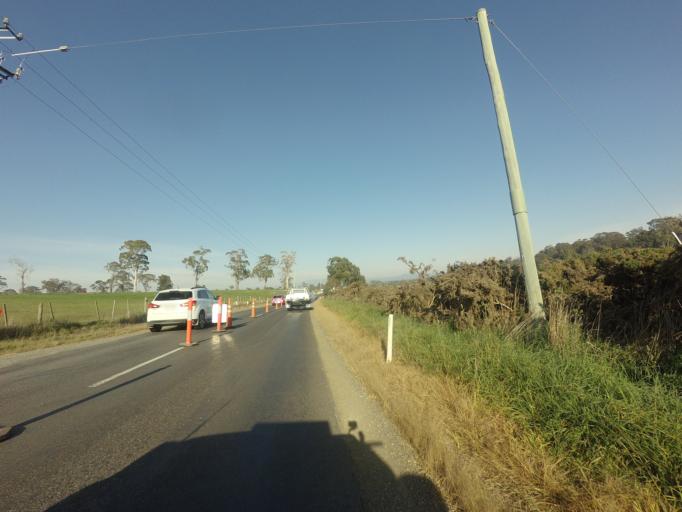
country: AU
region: Tasmania
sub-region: Northern Midlands
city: Longford
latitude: -41.5575
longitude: 146.9865
